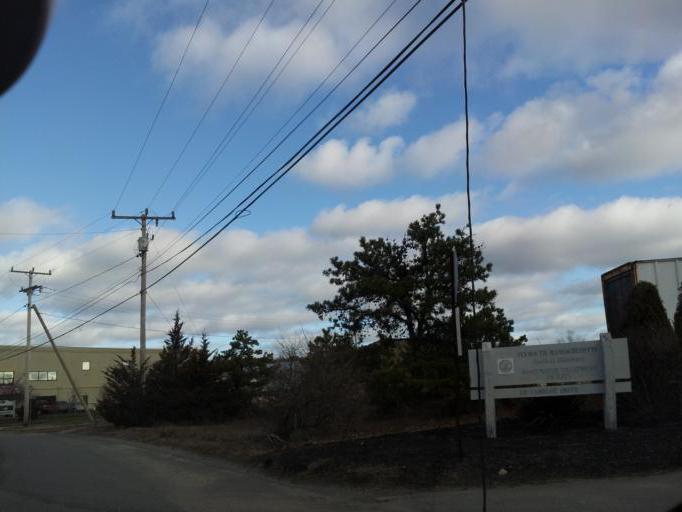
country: US
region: Massachusetts
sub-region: Plymouth County
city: Plymouth
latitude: 41.9281
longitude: -70.6459
